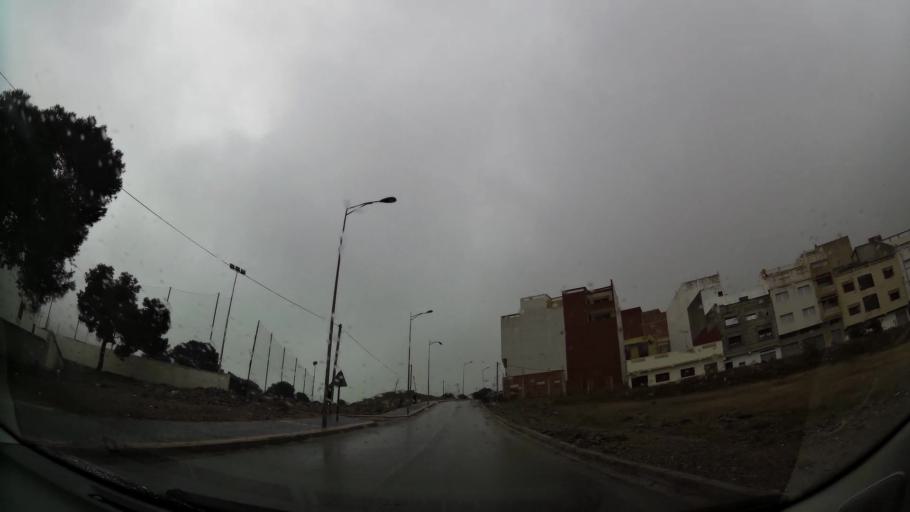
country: MA
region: Taza-Al Hoceima-Taounate
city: Al Hoceima
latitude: 35.2475
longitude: -3.9456
